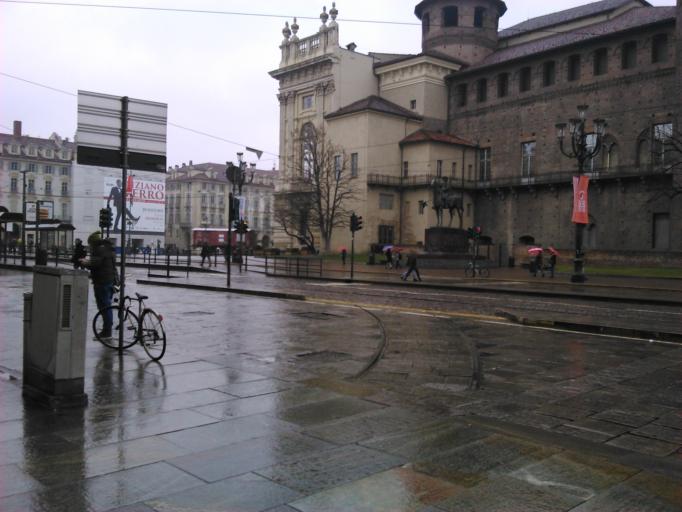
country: IT
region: Piedmont
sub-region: Provincia di Torino
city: Turin
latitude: 45.0701
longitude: 7.6858
